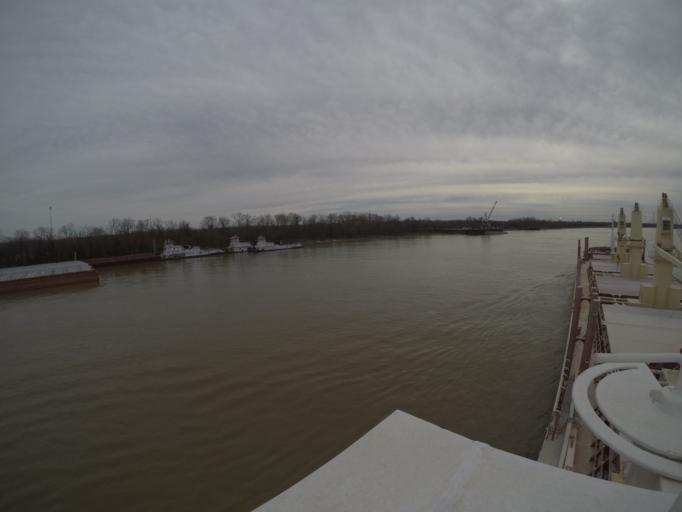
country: US
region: Louisiana
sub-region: Saint John the Baptist Parish
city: Laplace
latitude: 30.0422
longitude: -90.4744
